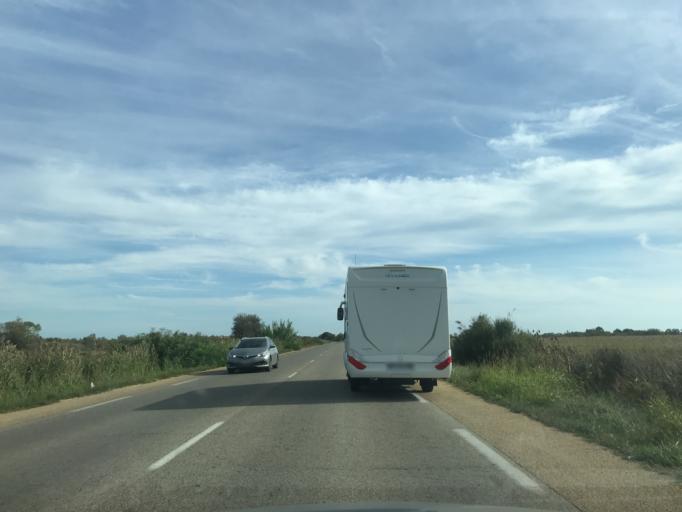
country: FR
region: Provence-Alpes-Cote d'Azur
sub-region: Departement des Bouches-du-Rhone
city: Saintes-Maries-de-la-Mer
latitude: 43.5094
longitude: 4.3990
